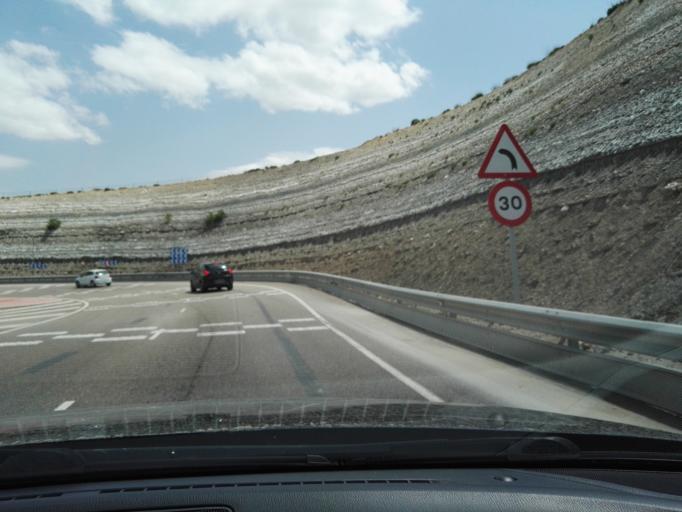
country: ES
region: Aragon
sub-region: Provincia de Zaragoza
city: Montecanal
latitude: 41.6177
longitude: -0.9617
